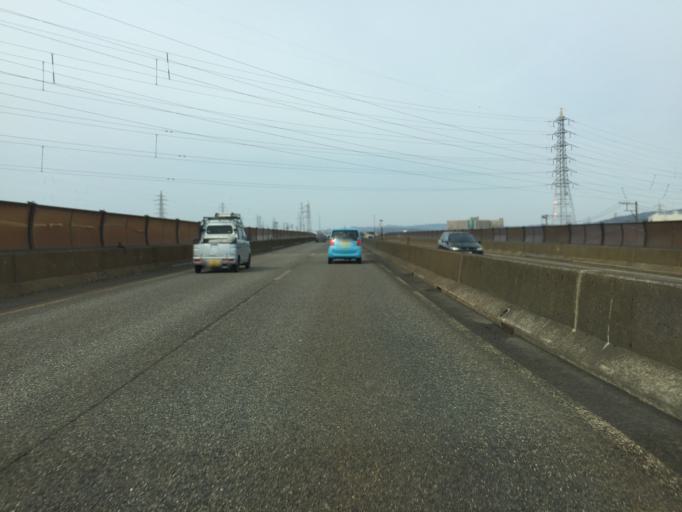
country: JP
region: Niigata
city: Nagaoka
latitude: 37.4425
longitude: 138.8701
